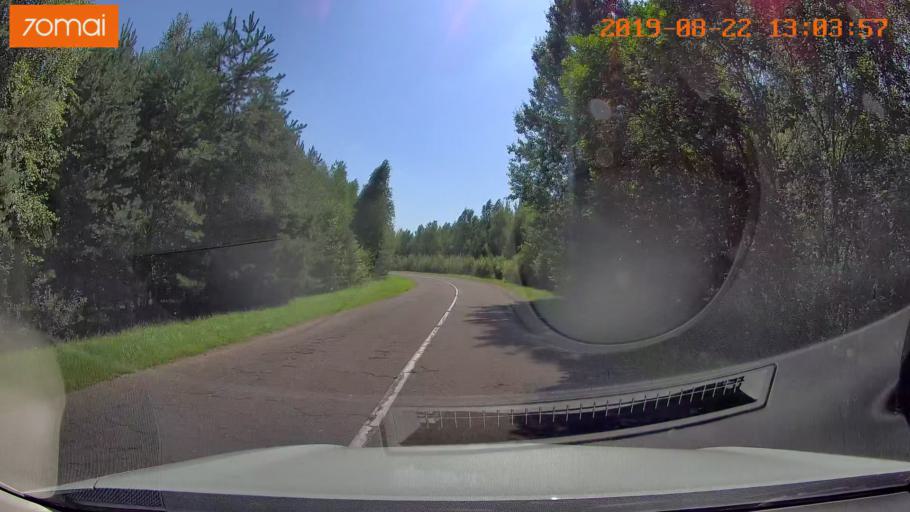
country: BY
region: Minsk
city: Prawdzinski
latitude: 53.3756
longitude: 27.8214
